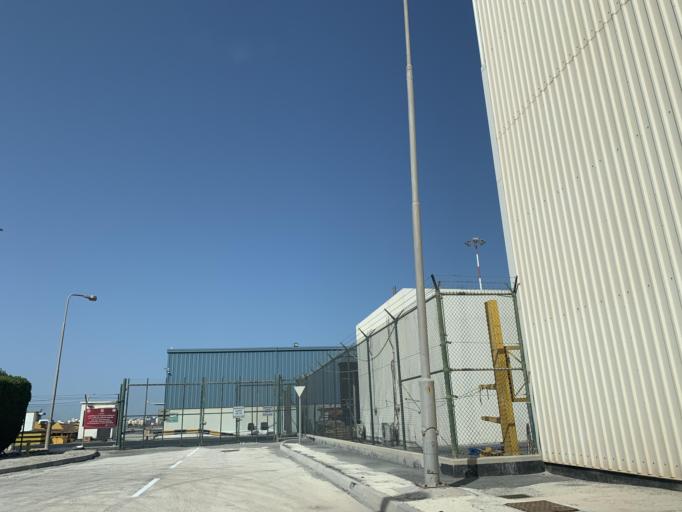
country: BH
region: Muharraq
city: Al Muharraq
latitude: 26.2737
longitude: 50.6194
